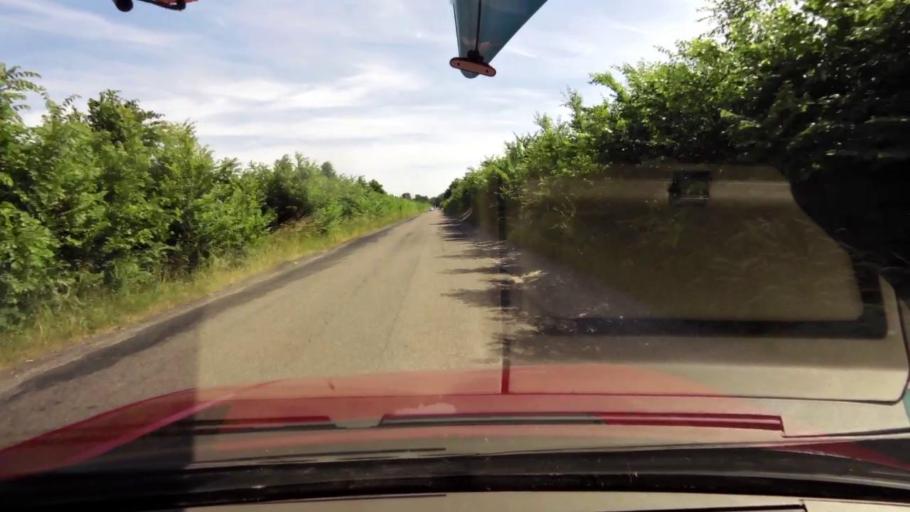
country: PL
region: Pomeranian Voivodeship
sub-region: Powiat slupski
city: Kobylnica
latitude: 54.3627
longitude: 16.9674
